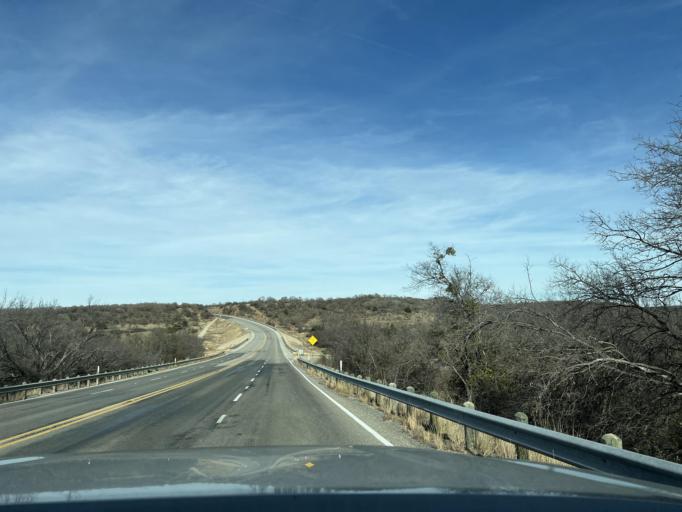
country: US
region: Texas
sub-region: Eastland County
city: Cisco
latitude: 32.4353
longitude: -98.9822
